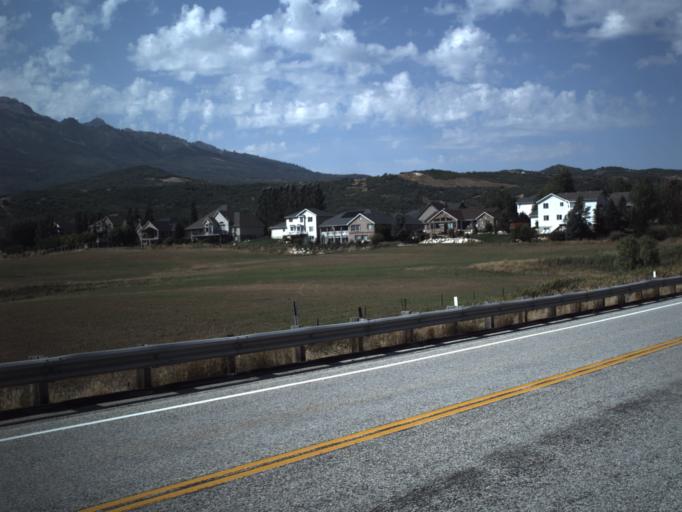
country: US
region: Utah
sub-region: Morgan County
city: Mountain Green
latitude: 41.1571
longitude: -111.7972
